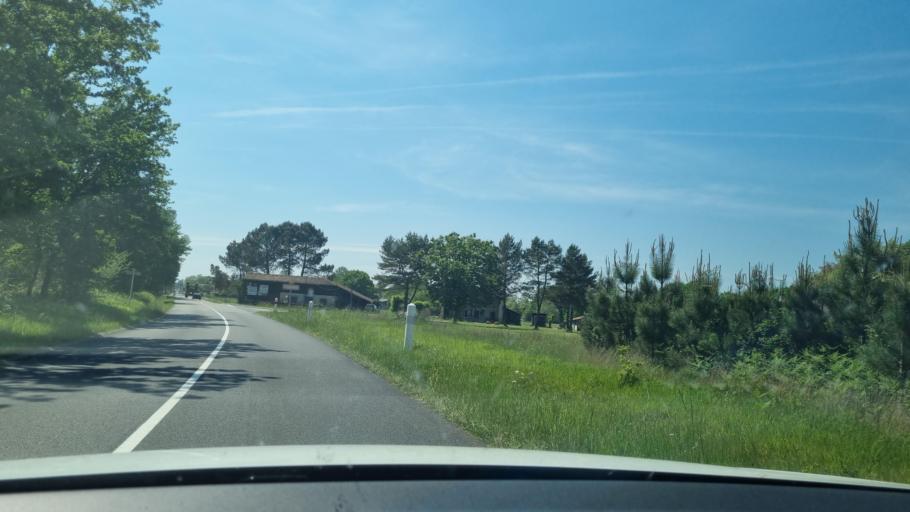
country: FR
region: Aquitaine
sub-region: Departement de la Gironde
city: Bazas
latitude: 44.2927
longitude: -0.2452
